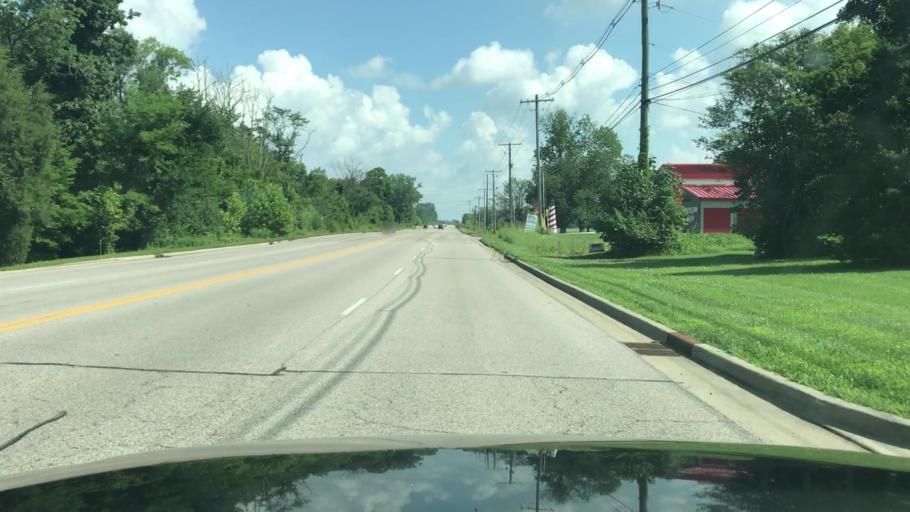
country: US
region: Indiana
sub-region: Vanderburgh County
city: Melody Hill
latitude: 38.0170
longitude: -87.4922
